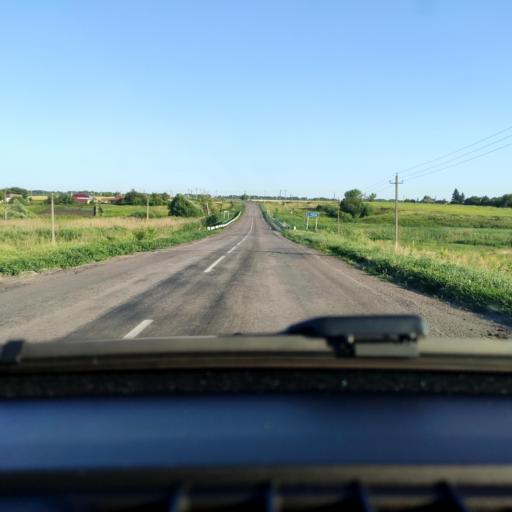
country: RU
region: Voronezj
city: Kashirskoye
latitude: 51.5002
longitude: 39.8337
